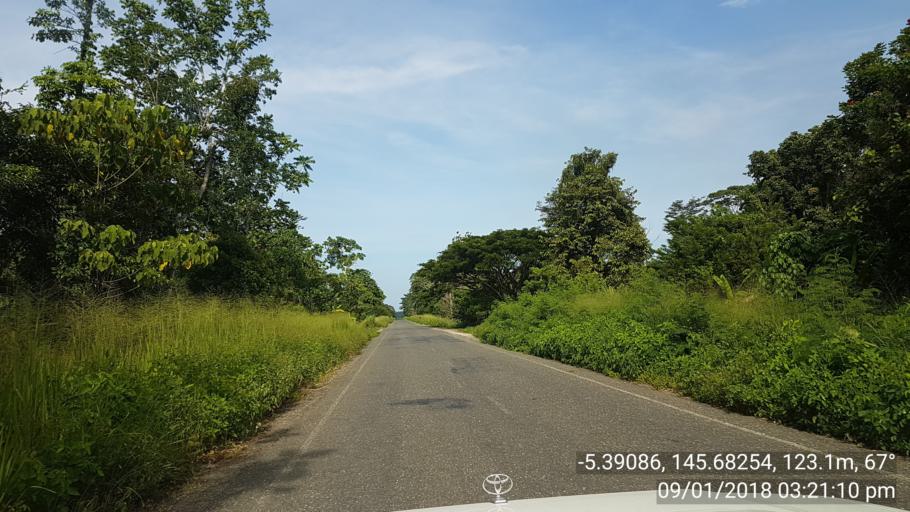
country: PG
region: Madang
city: Madang
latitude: -5.3908
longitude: 145.6825
